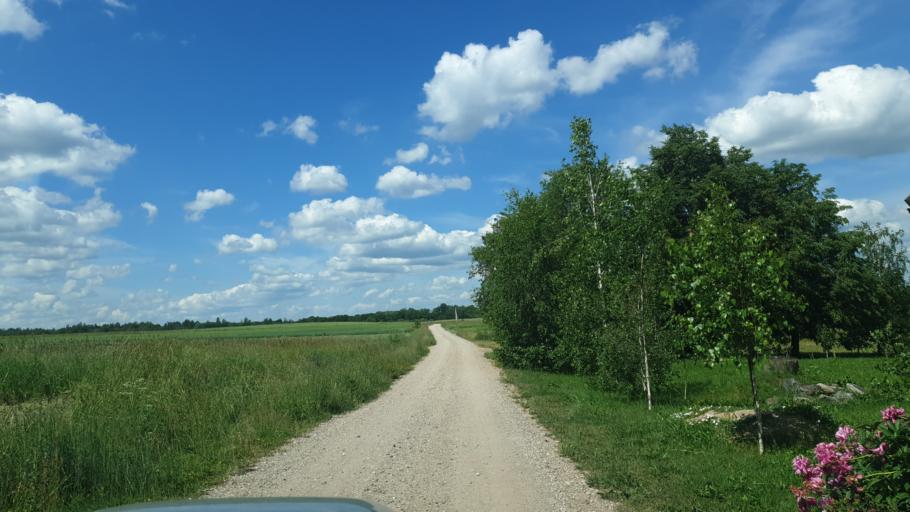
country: LT
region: Vilnius County
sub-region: Vilniaus Rajonas
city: Vievis
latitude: 54.8208
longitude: 24.9519
